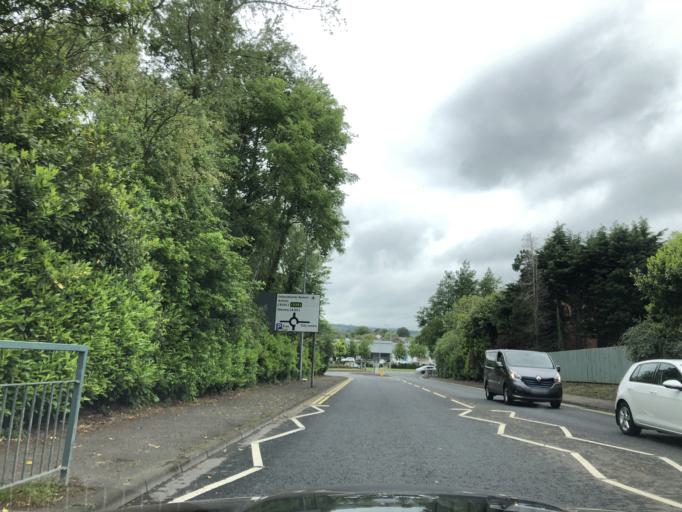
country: GB
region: Northern Ireland
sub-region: Lisburn District
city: Lisburn
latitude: 54.5144
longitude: -6.0541
